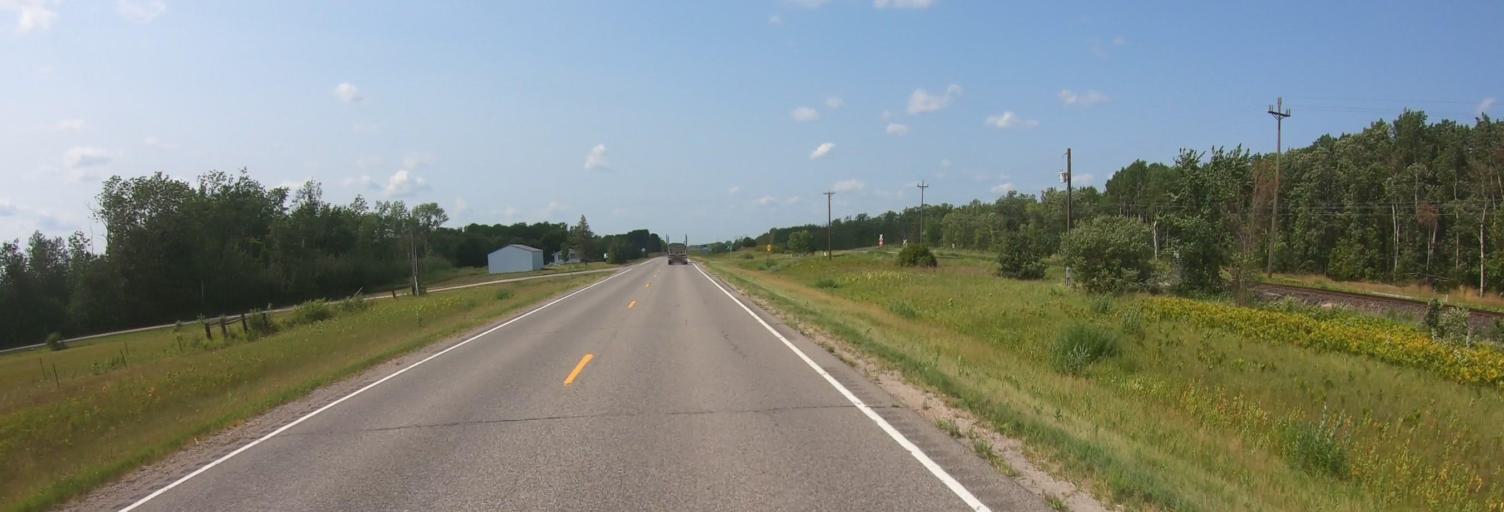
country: US
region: Minnesota
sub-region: Roseau County
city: Warroad
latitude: 48.8349
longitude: -95.1769
